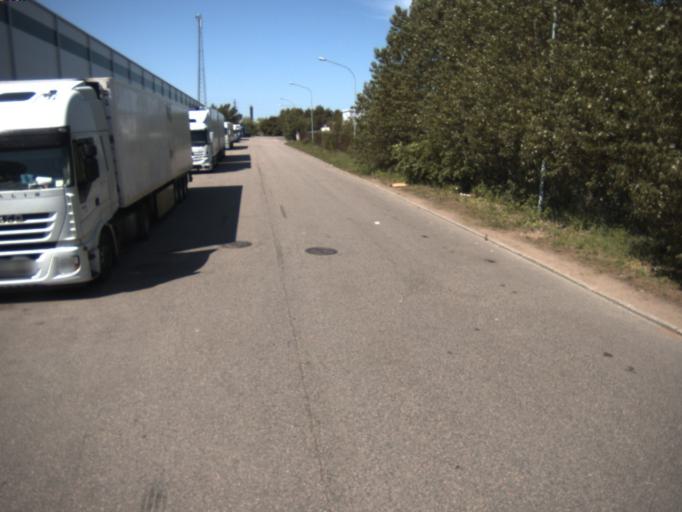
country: SE
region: Skane
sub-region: Helsingborg
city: Gantofta
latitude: 56.0145
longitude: 12.7702
